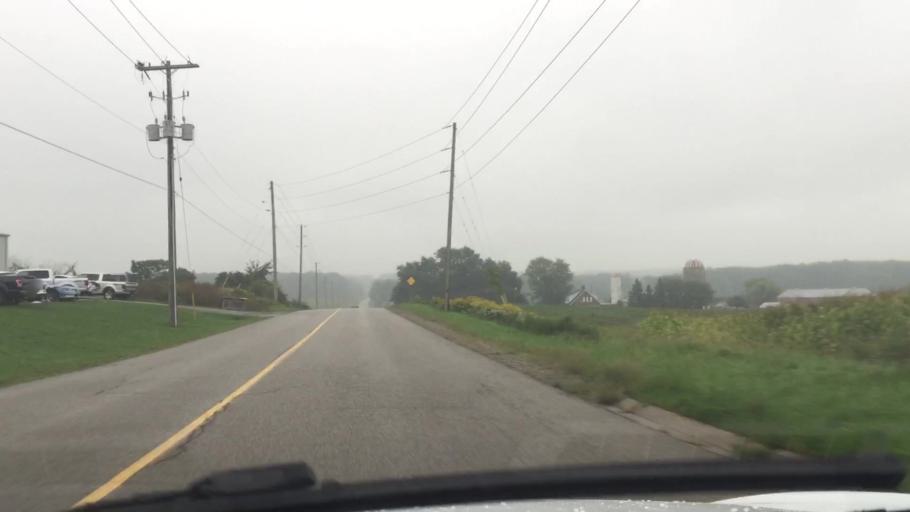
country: CA
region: Ontario
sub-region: Oxford County
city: Woodstock
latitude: 43.1106
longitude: -80.7185
